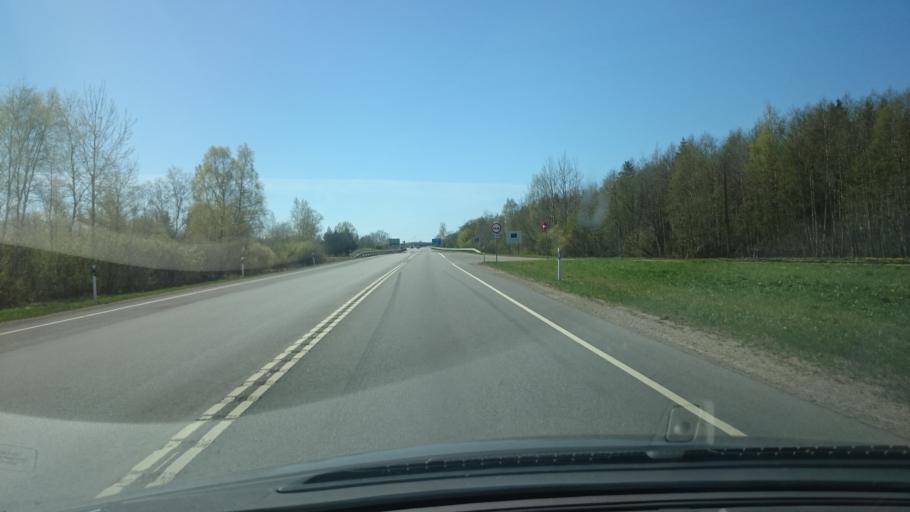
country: EE
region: Ida-Virumaa
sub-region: Johvi vald
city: Johvi
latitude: 59.3683
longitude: 27.4098
